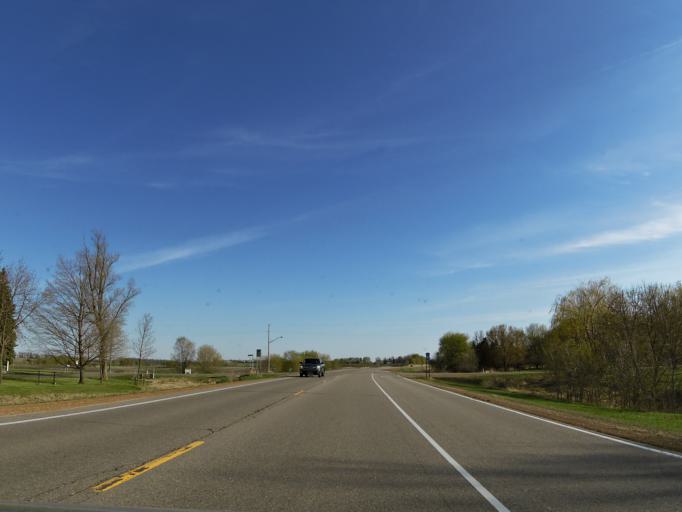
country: US
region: Minnesota
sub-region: Scott County
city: Prior Lake
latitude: 44.6535
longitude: -93.4995
